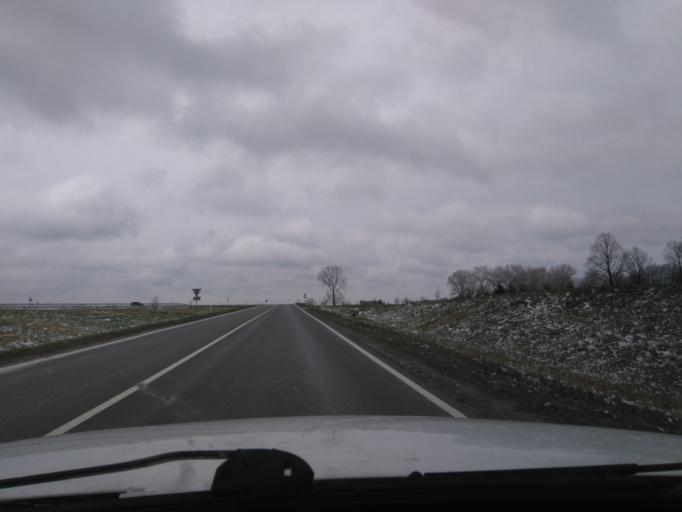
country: LT
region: Marijampoles apskritis
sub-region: Marijampole Municipality
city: Marijampole
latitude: 54.5749
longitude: 23.2987
